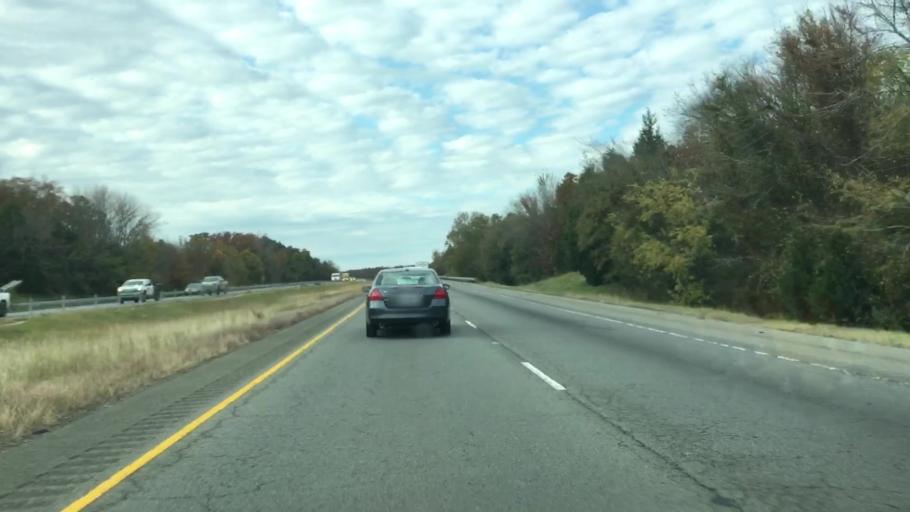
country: US
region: Arkansas
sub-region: Faulkner County
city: Conway
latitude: 35.1322
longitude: -92.5163
